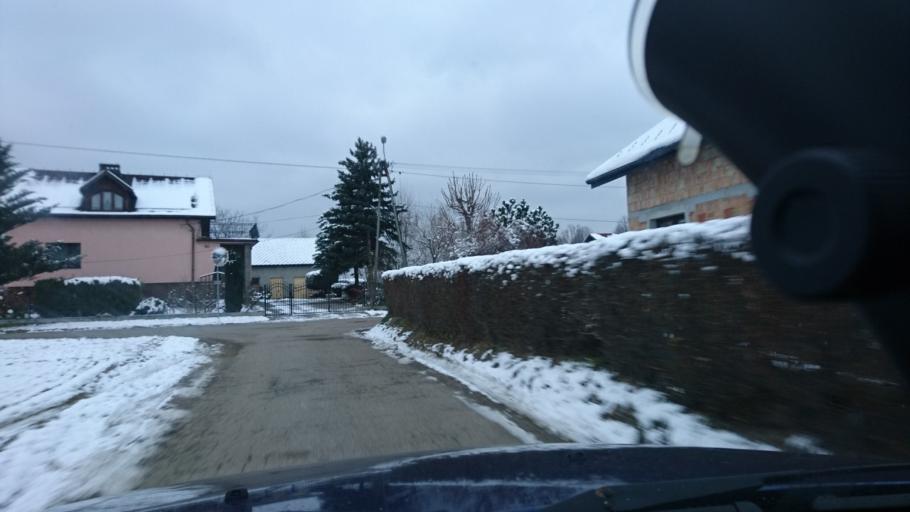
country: PL
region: Silesian Voivodeship
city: Janowice
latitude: 49.8647
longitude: 19.1098
